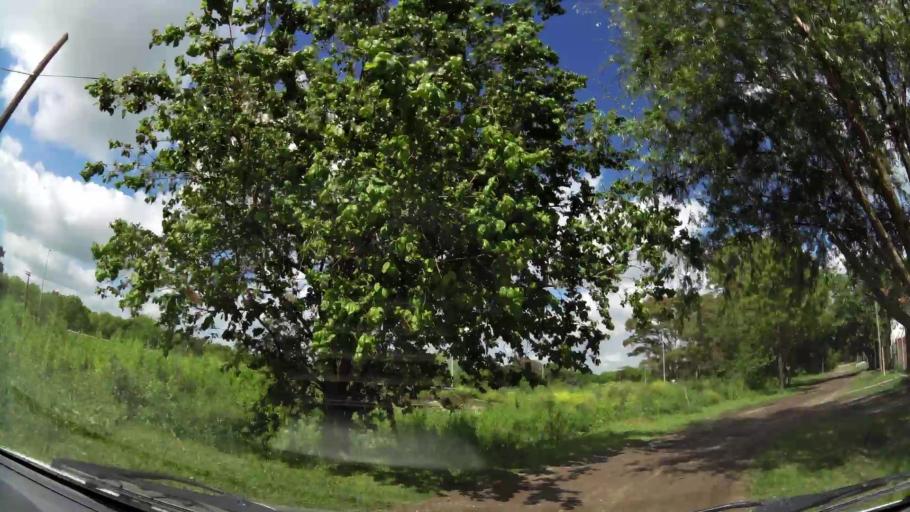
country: AR
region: Buenos Aires
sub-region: Partido de Quilmes
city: Quilmes
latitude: -34.8395
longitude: -58.1777
